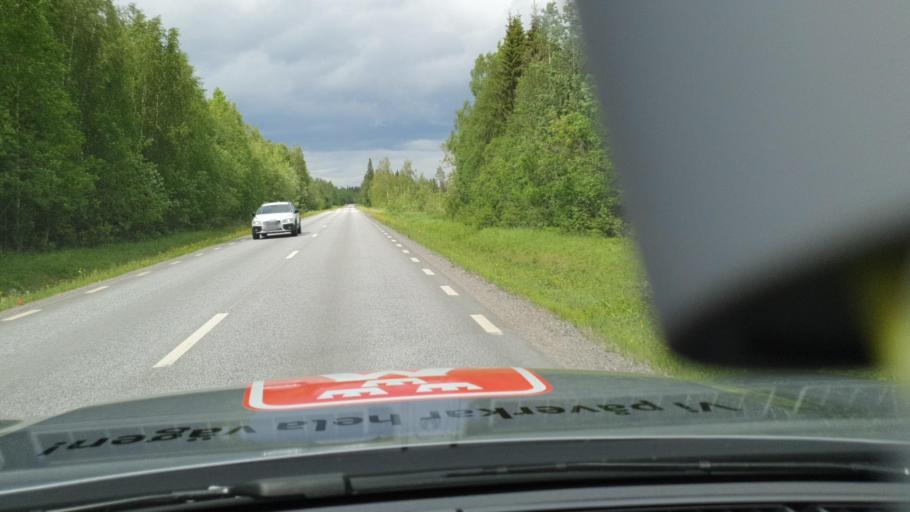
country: SE
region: Norrbotten
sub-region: Lulea Kommun
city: Lulea
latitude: 65.6784
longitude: 22.2174
